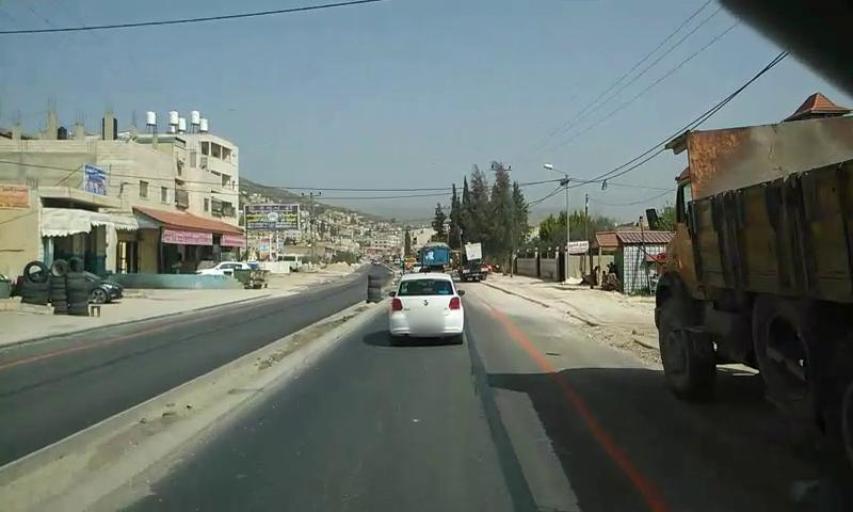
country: PS
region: West Bank
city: Huwwarah
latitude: 32.1433
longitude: 35.2581
